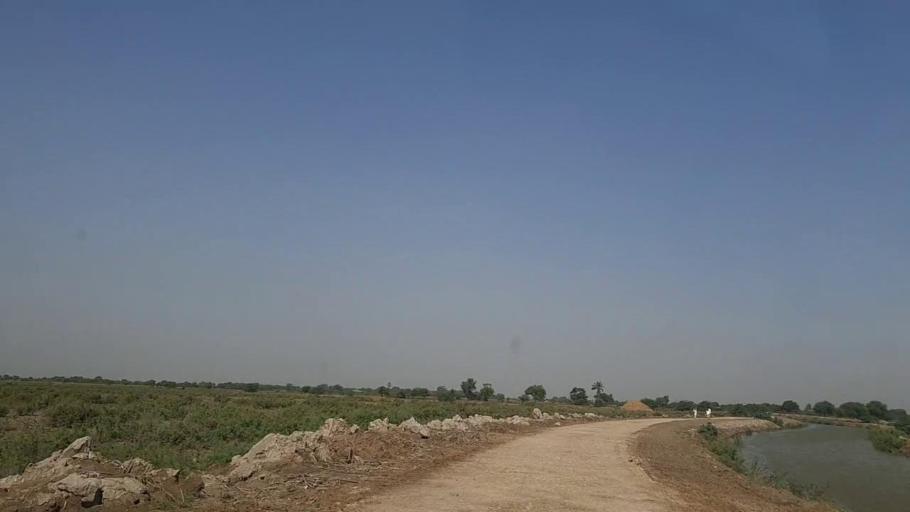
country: PK
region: Sindh
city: Daro Mehar
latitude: 24.7556
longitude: 68.1358
